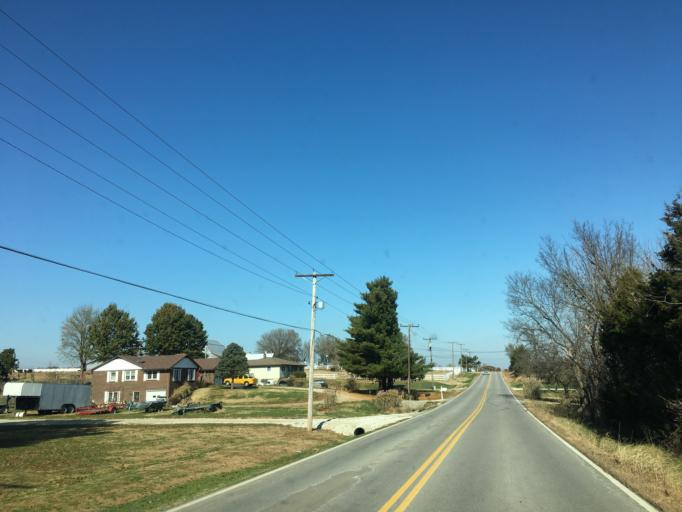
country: US
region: Missouri
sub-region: Cole County
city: Wardsville
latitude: 38.5015
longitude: -92.1761
